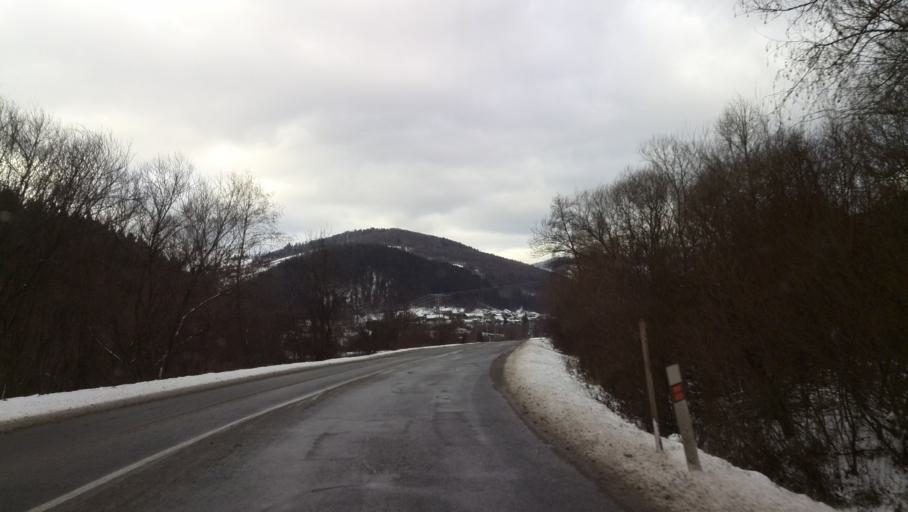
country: SK
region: Kosicky
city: Gelnica
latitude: 48.8666
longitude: 20.9738
